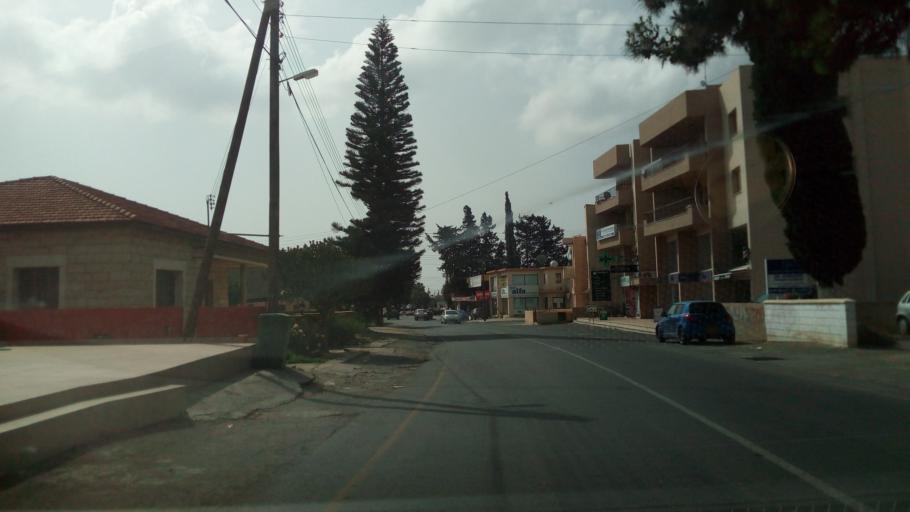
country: CY
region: Limassol
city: Ypsonas
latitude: 34.6853
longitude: 32.9635
